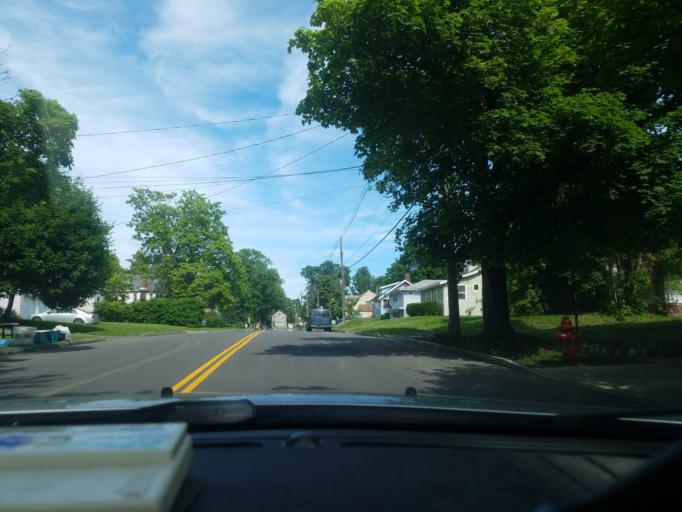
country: US
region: New York
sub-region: Onondaga County
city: East Syracuse
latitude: 43.0484
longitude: -76.1067
